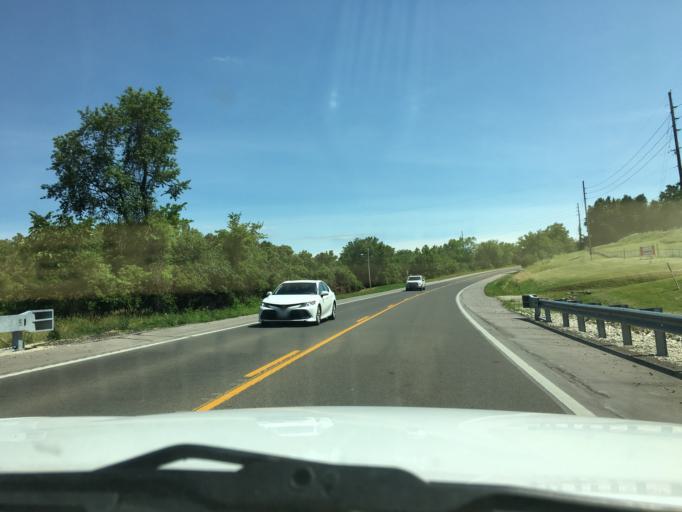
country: US
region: Missouri
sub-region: Franklin County
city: Union
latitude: 38.4980
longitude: -91.0032
